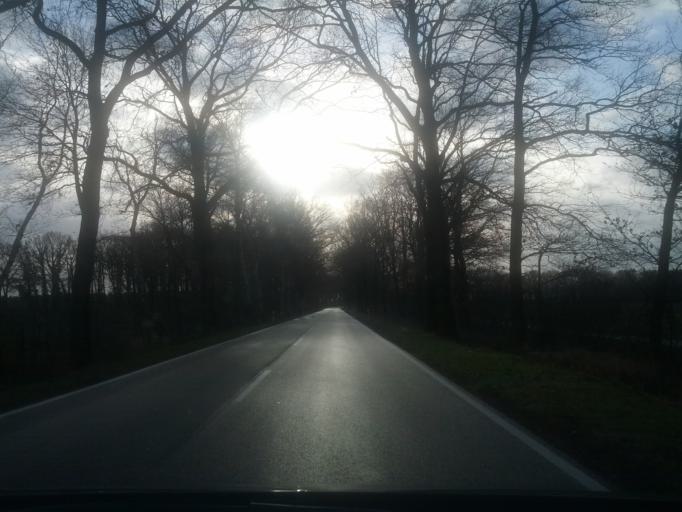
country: DE
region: Lower Saxony
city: Hamersen
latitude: 53.2425
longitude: 9.4844
